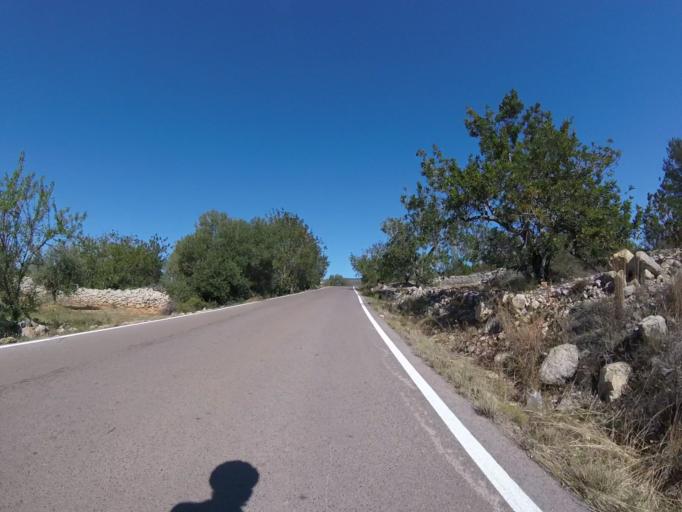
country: ES
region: Valencia
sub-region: Provincia de Castello
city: Santa Magdalena de Pulpis
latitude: 40.3741
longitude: 0.2720
